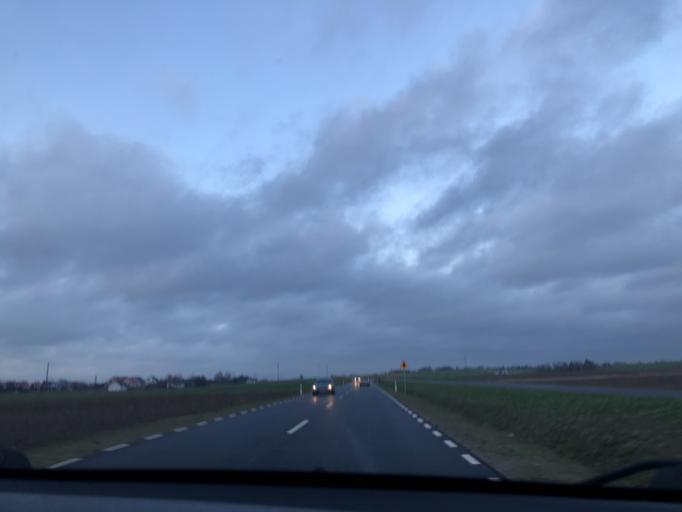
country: PL
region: Podlasie
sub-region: Lomza
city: Lomza
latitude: 53.1401
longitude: 22.0514
